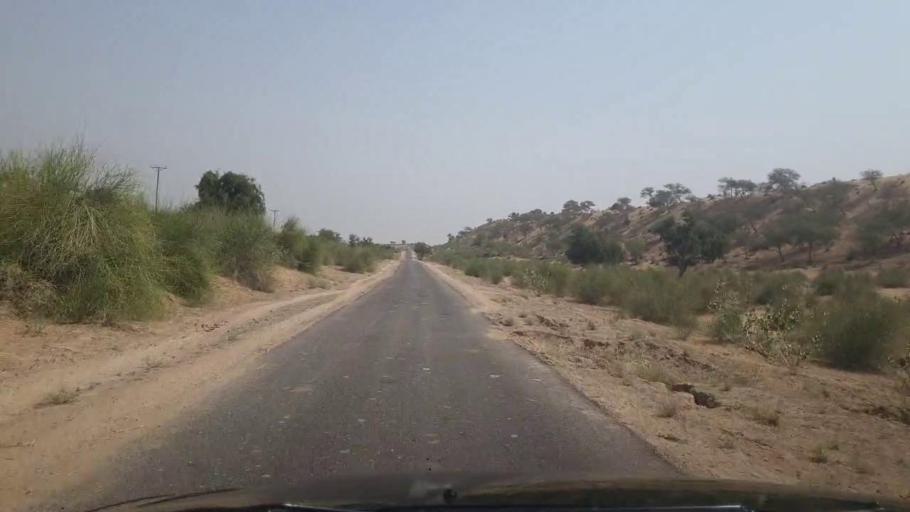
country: PK
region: Sindh
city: Islamkot
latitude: 24.9452
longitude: 70.4141
